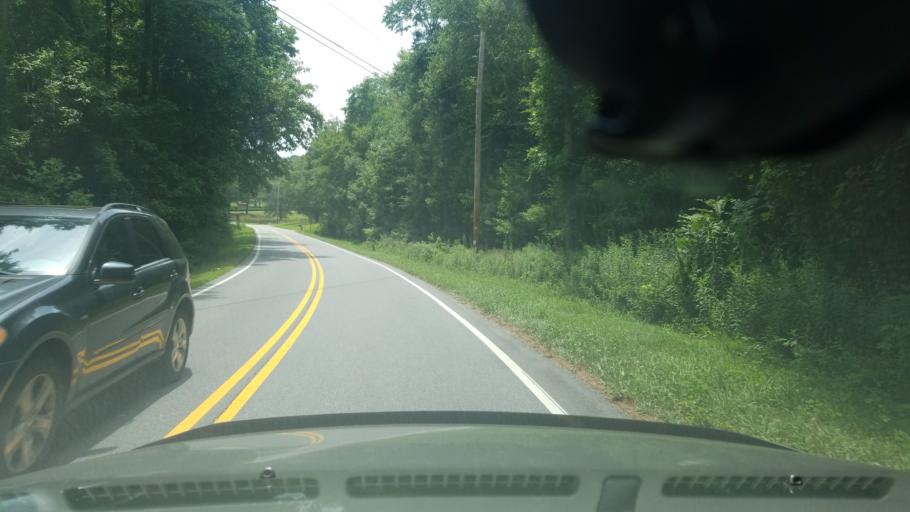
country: US
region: Georgia
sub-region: Forsyth County
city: Cumming
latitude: 34.1929
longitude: -84.2099
